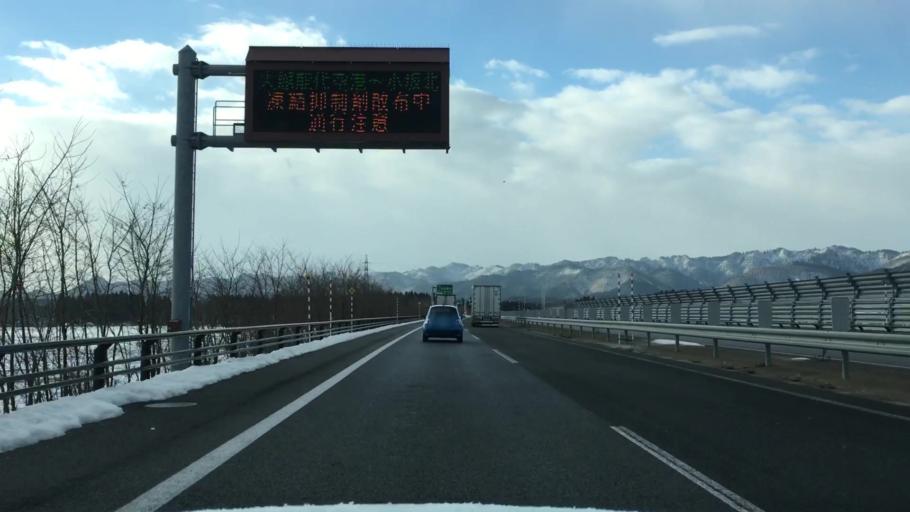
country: JP
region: Akita
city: Odate
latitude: 40.2551
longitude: 140.5199
